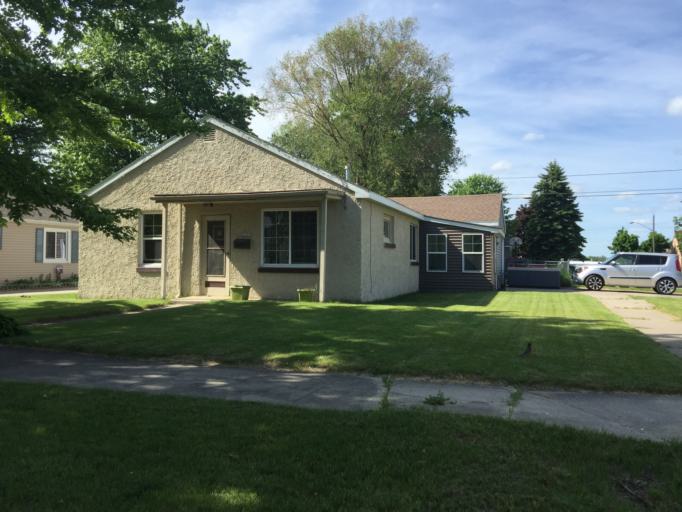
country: US
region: Wisconsin
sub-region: Marinette County
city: Marinette
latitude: 45.1135
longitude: -87.6313
